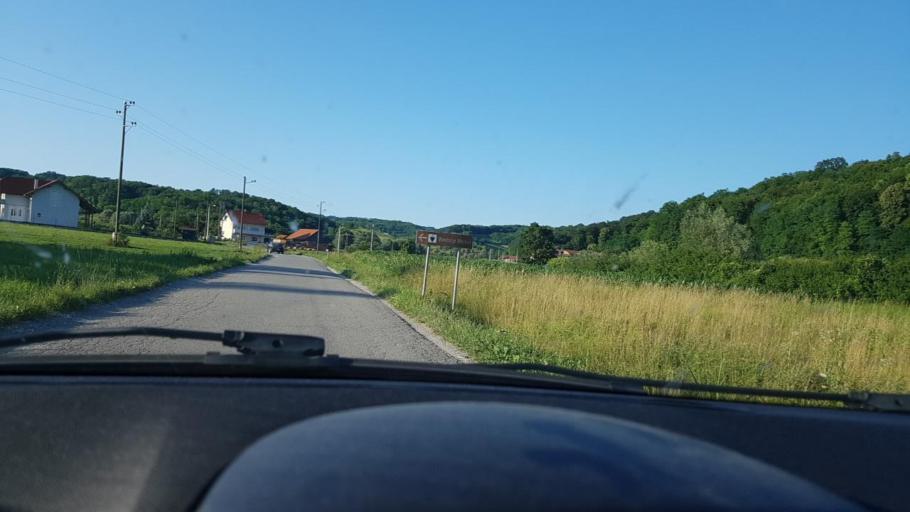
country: HR
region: Krapinsko-Zagorska
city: Zabok
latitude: 46.0785
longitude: 15.9283
